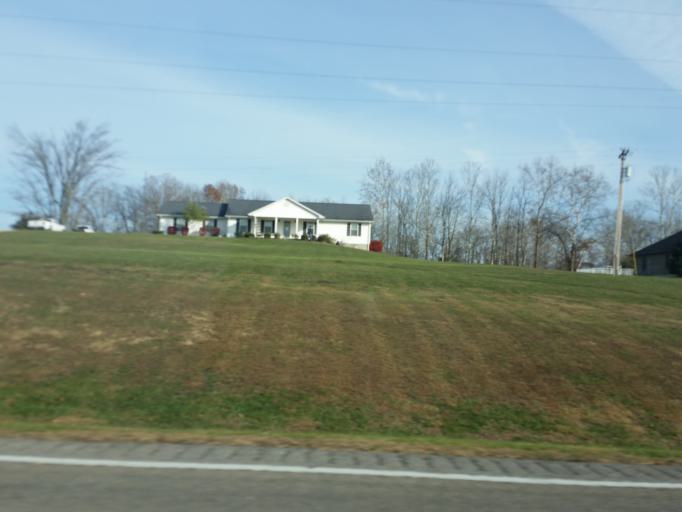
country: US
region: Kentucky
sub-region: Pendleton County
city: Falmouth
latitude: 38.6096
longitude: -84.3041
